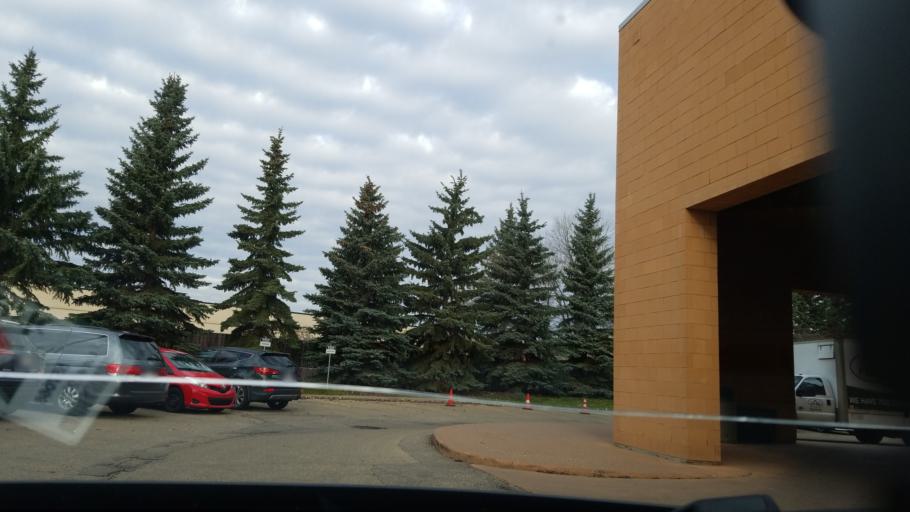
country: CA
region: Alberta
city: Edmonton
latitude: 53.6145
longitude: -113.4891
